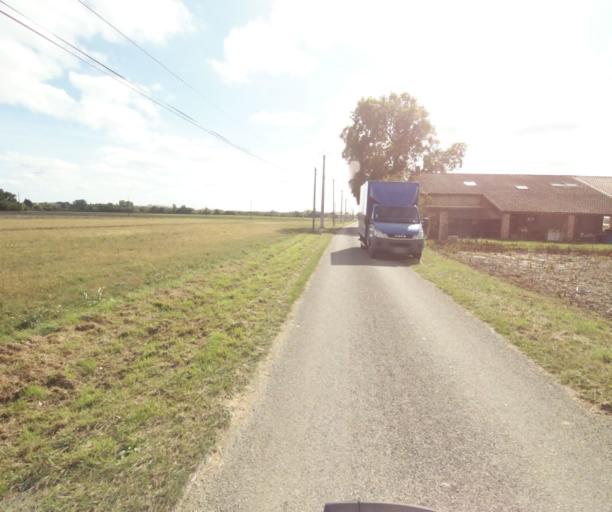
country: FR
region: Midi-Pyrenees
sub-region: Departement du Tarn-et-Garonne
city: Finhan
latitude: 43.9382
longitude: 1.2064
